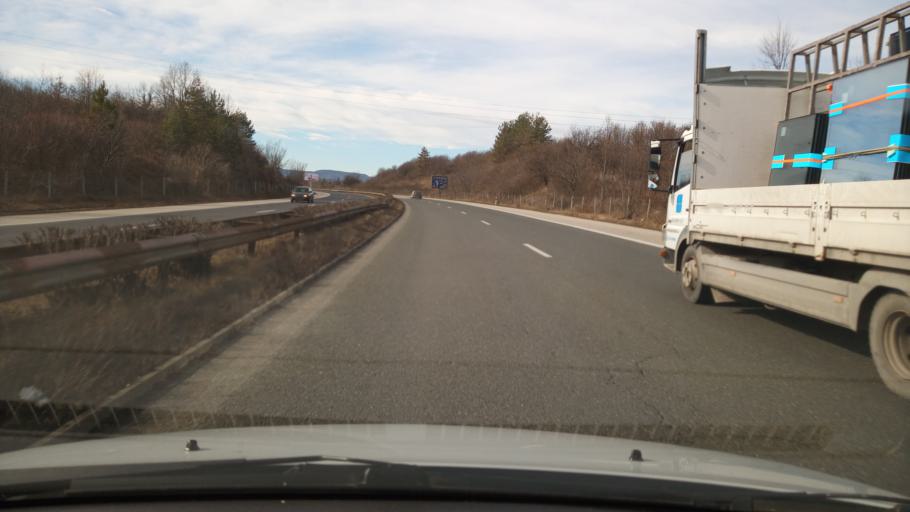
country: BG
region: Sofiya
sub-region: Obshtina Pravets
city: Pravets
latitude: 42.9507
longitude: 24.0014
